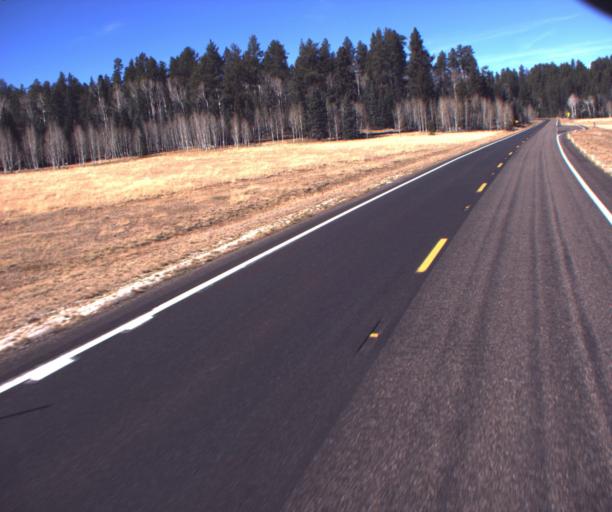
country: US
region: Arizona
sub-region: Coconino County
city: Grand Canyon
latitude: 36.5299
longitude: -112.1505
